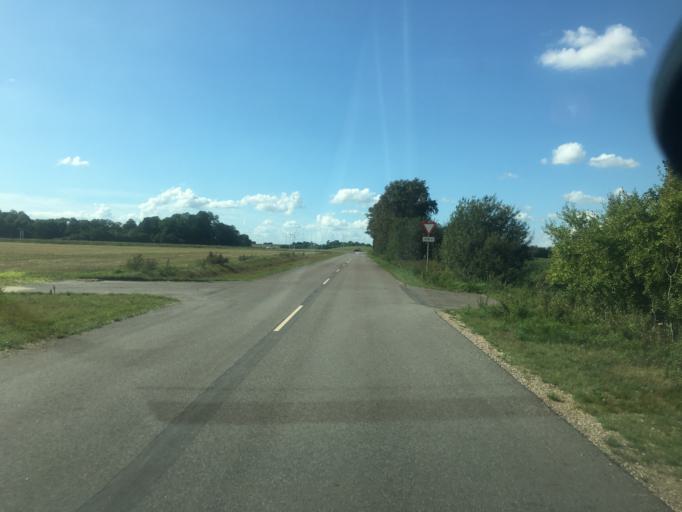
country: DE
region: Schleswig-Holstein
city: Ellhoft
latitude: 54.9682
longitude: 8.9702
